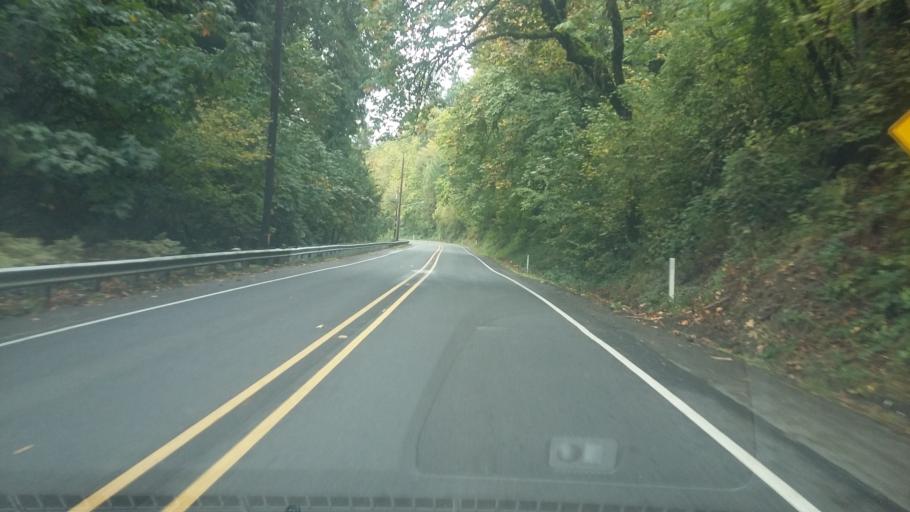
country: US
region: Washington
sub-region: Clark County
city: Ridgefield
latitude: 45.8161
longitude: -122.7200
